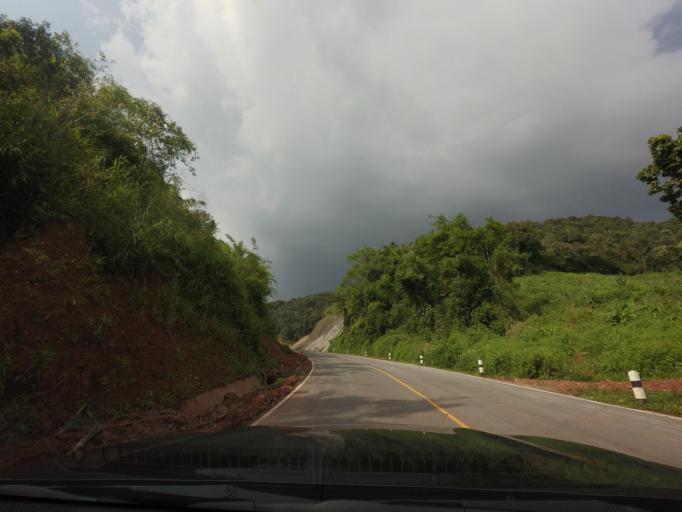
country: TH
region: Nan
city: Bo Kluea
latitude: 19.2403
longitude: 101.1816
